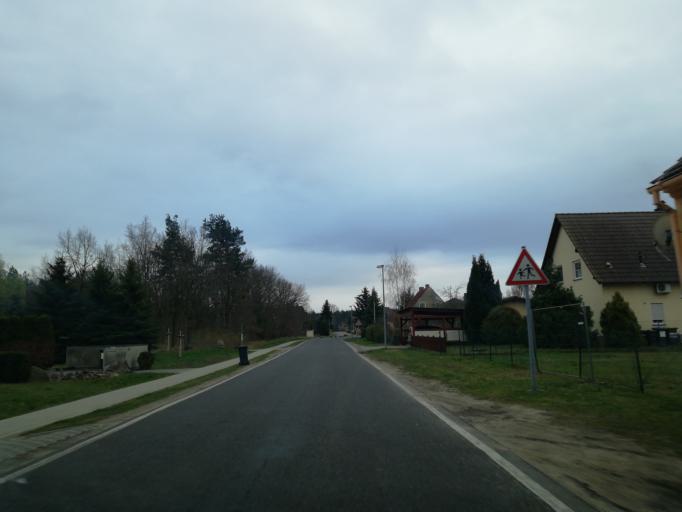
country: DE
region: Brandenburg
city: Vetschau
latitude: 51.7647
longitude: 14.1316
